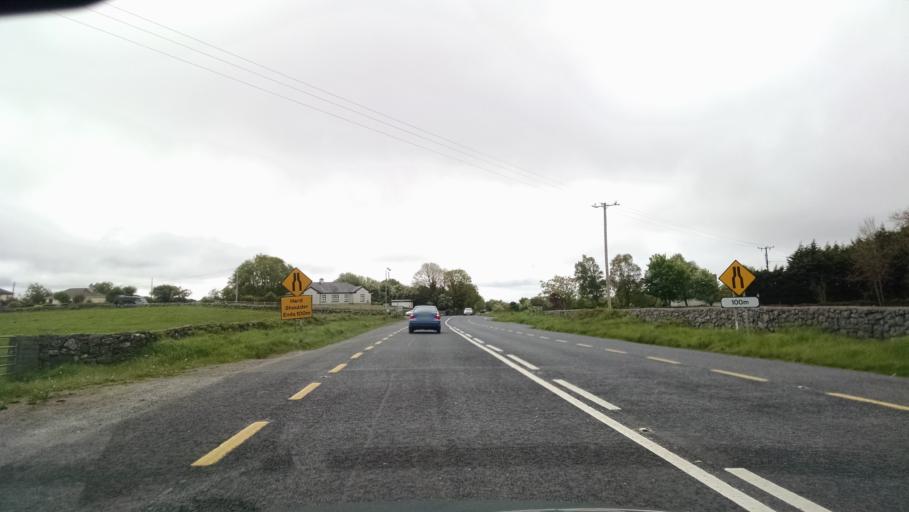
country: IE
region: Connaught
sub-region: County Galway
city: Claregalway
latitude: 53.4049
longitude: -9.0171
